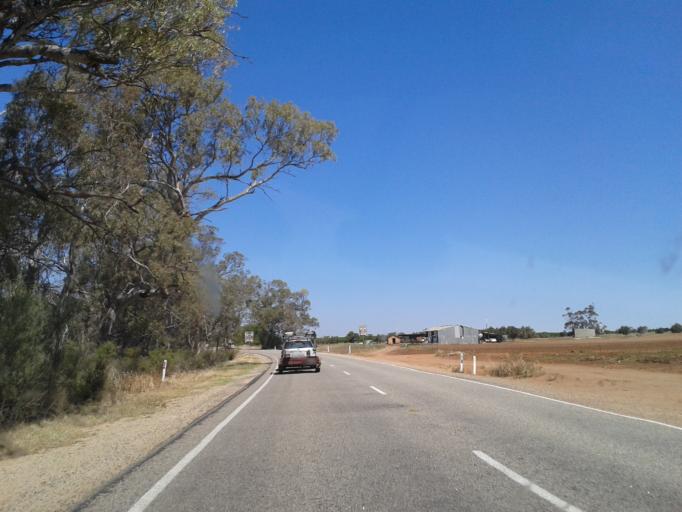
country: AU
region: Victoria
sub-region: Swan Hill
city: Swan Hill
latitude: -35.1111
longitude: 143.3485
